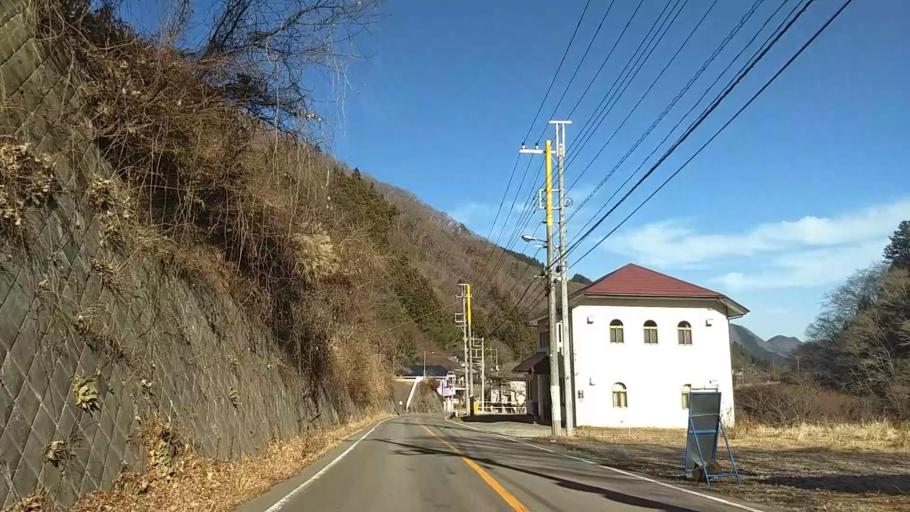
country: JP
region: Yamanashi
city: Otsuki
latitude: 35.5255
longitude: 139.0259
